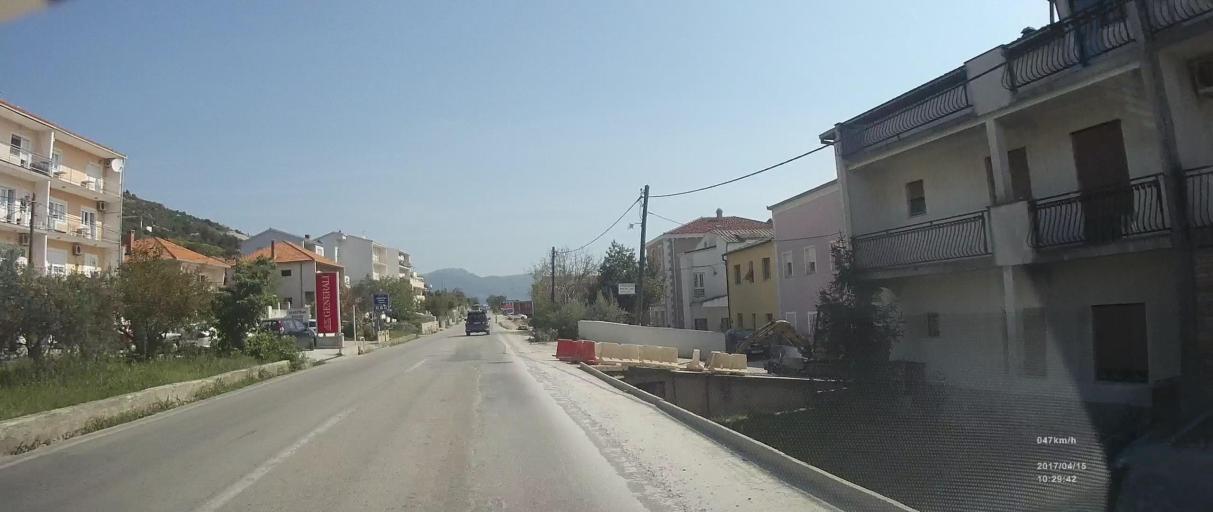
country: HR
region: Splitsko-Dalmatinska
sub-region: Grad Trogir
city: Trogir
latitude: 43.5251
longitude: 16.2684
